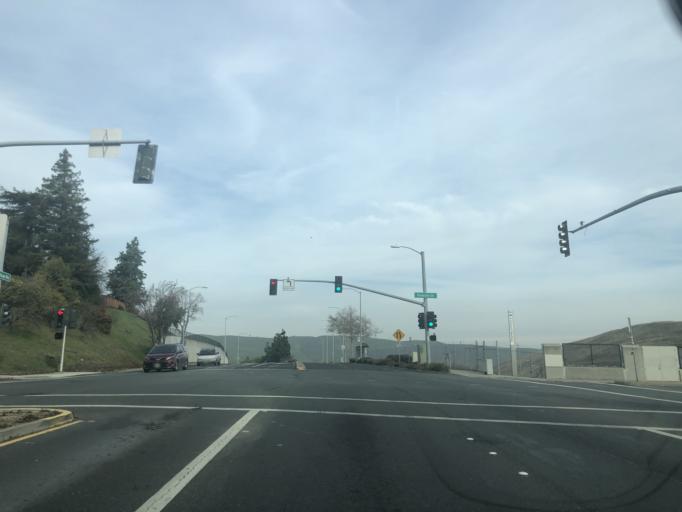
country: US
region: California
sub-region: Contra Costa County
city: Concord
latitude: 38.0041
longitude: -122.0242
